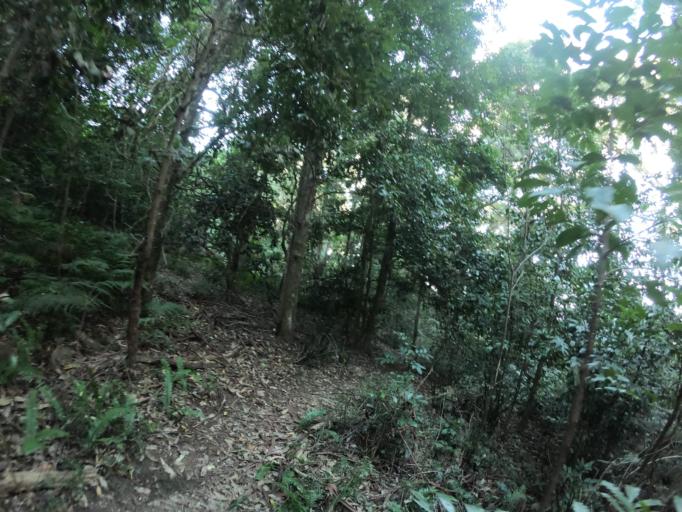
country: AU
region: New South Wales
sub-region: Wollongong
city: Mount Keira
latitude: -34.4100
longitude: 150.8360
